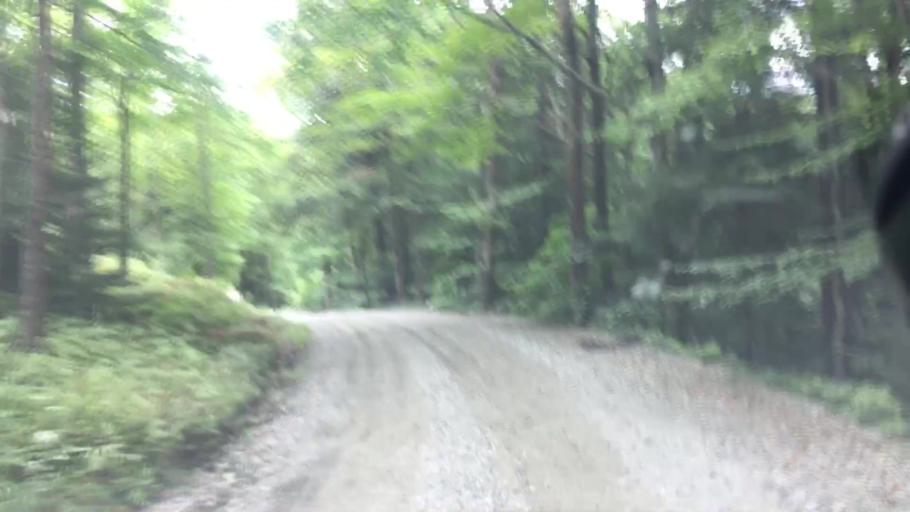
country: US
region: Vermont
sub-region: Windham County
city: Dover
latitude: 42.8375
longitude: -72.7678
